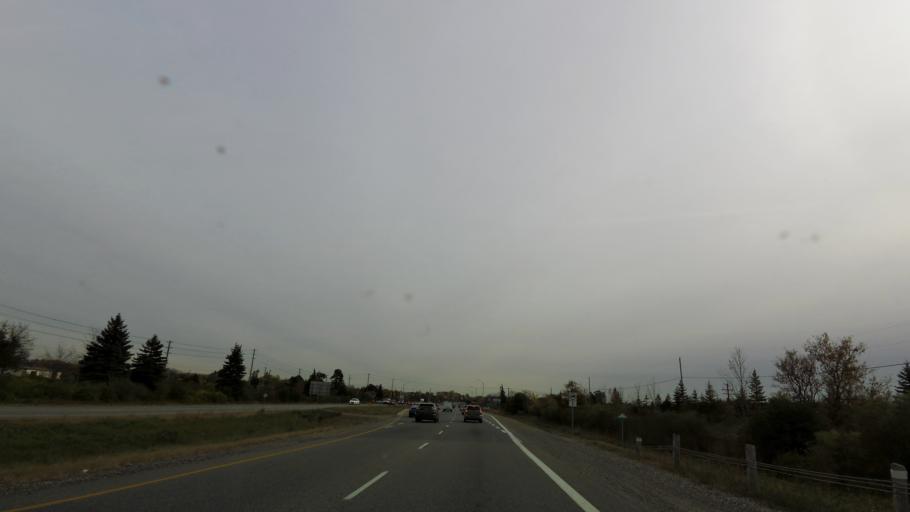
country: CA
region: Ontario
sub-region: Wellington County
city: Guelph
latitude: 43.5210
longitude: -80.2528
